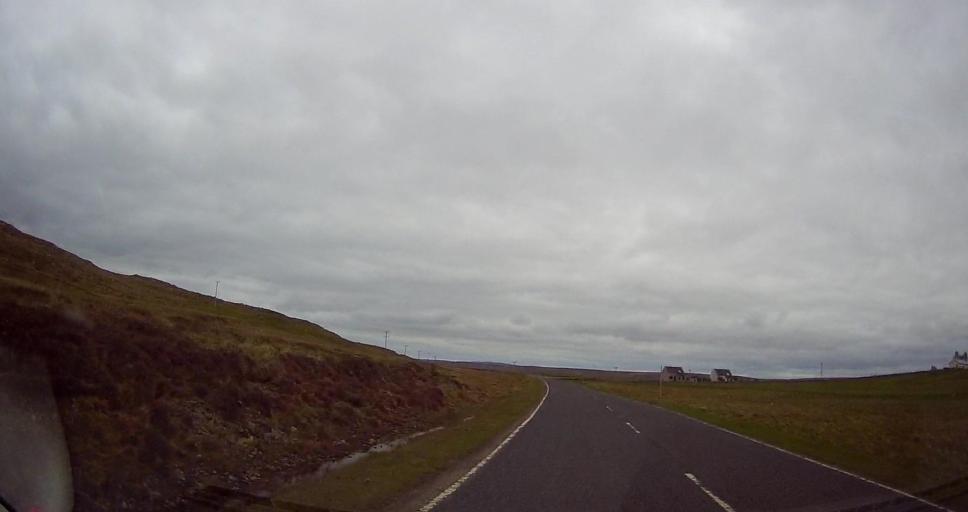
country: GB
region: Scotland
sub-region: Shetland Islands
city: Shetland
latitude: 60.6889
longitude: -0.9615
